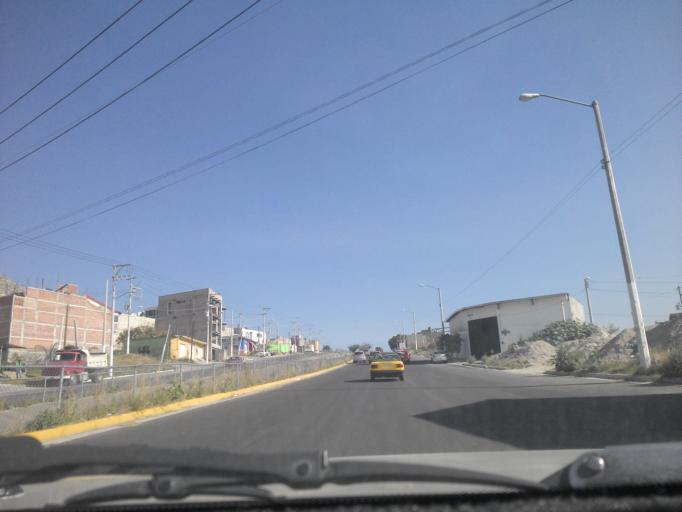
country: MX
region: Jalisco
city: Guadalajara
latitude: 20.6592
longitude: -103.4542
